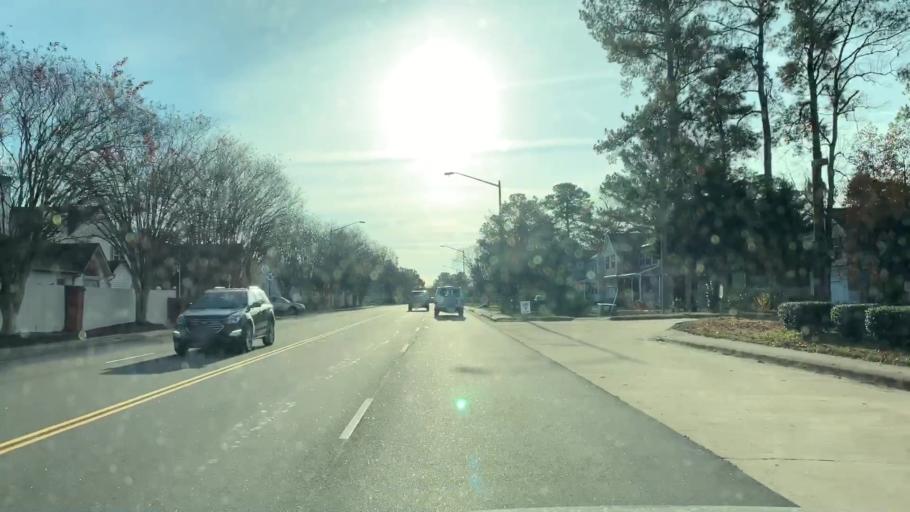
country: US
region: Virginia
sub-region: City of Chesapeake
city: Chesapeake
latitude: 36.7916
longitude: -76.1673
